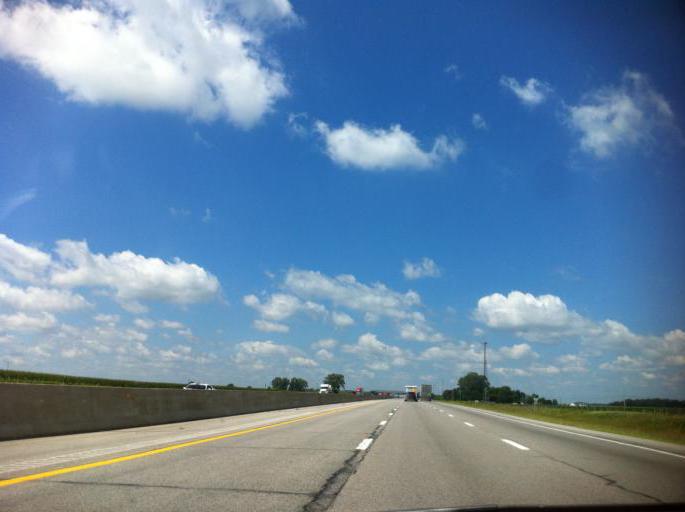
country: US
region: Ohio
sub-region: Sandusky County
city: Stony Prairie
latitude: 41.4272
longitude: -83.1913
